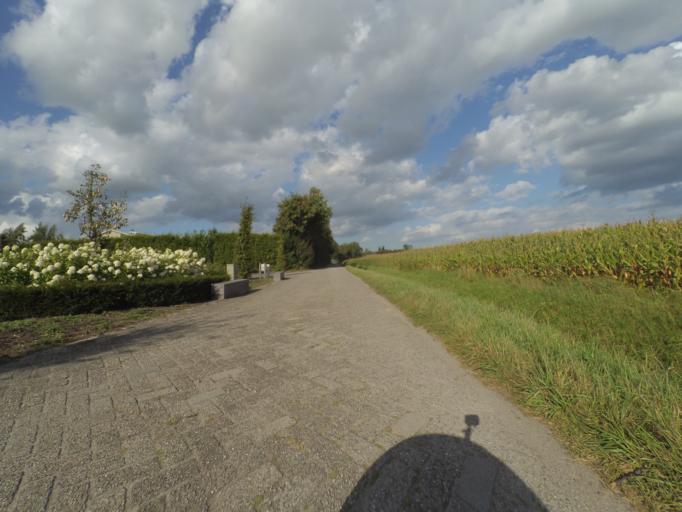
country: NL
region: Gelderland
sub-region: Gemeente Ede
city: Ederveen
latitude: 52.0720
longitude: 5.5818
